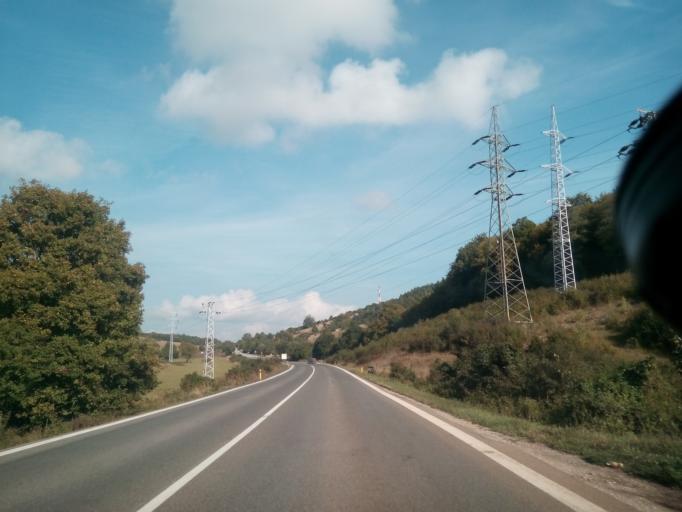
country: SK
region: Kosicky
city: Roznava
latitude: 48.6118
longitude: 20.6356
